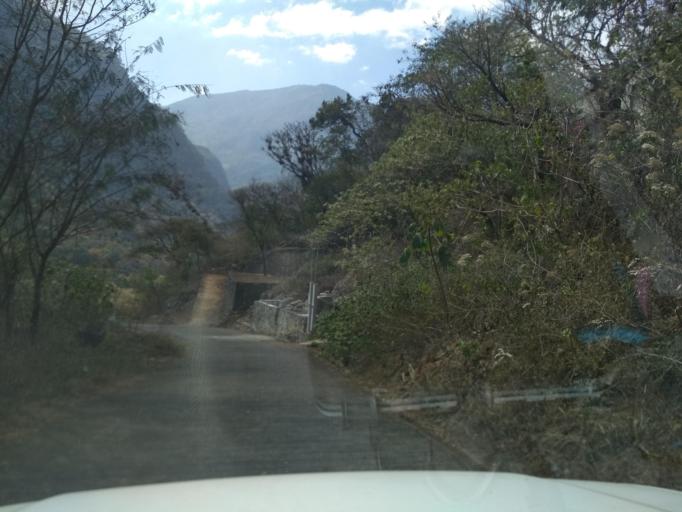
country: MX
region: Veracruz
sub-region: Tlilapan
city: Tonalixco
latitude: 18.7881
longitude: -97.0883
